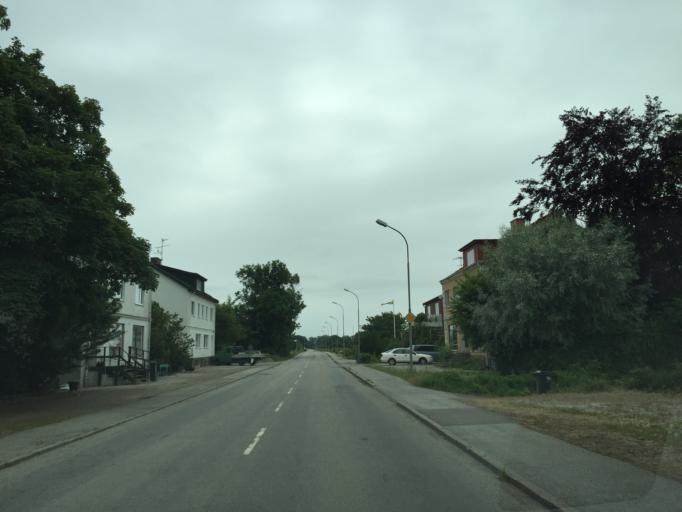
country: SE
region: Skane
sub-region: Ystads Kommun
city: Kopingebro
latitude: 55.4358
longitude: 14.1136
